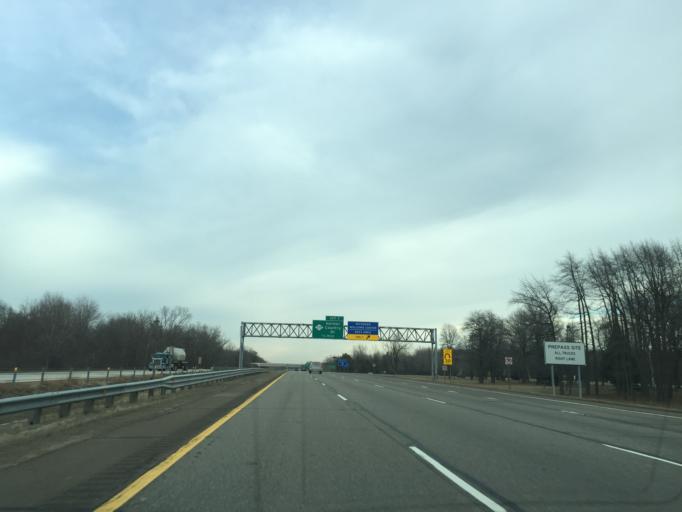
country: US
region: Michigan
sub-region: Berrien County
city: New Buffalo
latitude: 41.7661
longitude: -86.7421
